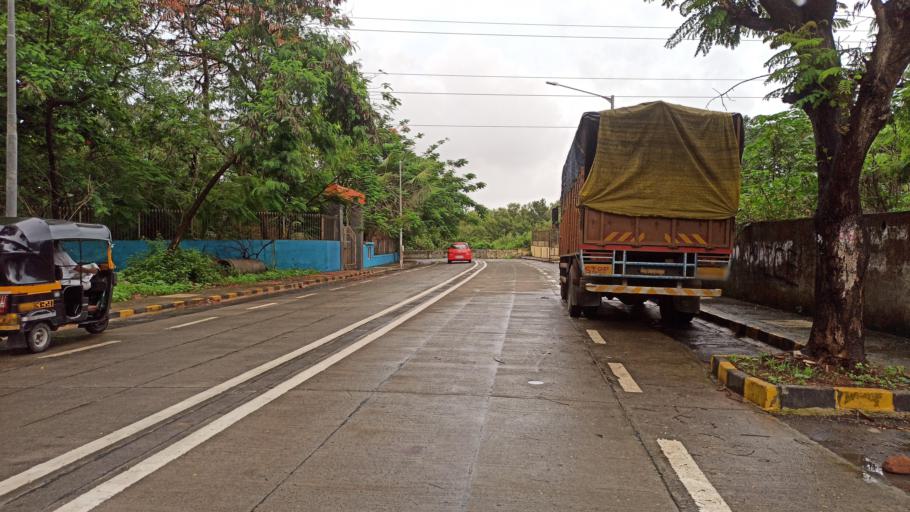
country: IN
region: Maharashtra
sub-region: Mumbai Suburban
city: Borivli
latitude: 19.2609
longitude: 72.8507
